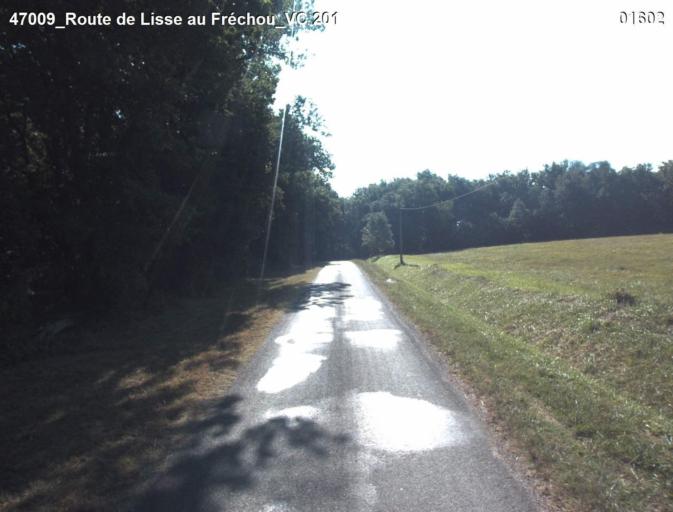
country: FR
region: Aquitaine
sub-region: Departement du Lot-et-Garonne
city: Mezin
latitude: 44.0931
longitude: 0.2925
